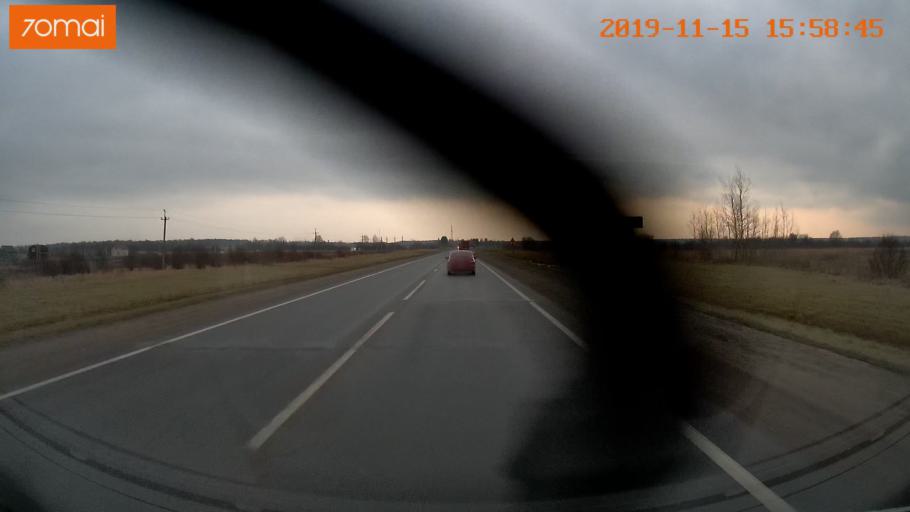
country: RU
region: Jaroslavl
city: Yaroslavl
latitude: 57.8155
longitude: 39.9528
